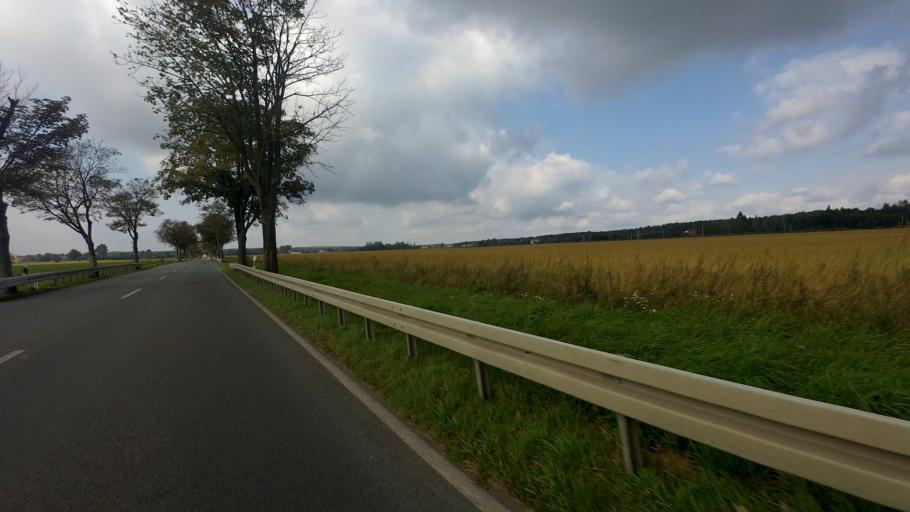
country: DE
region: Brandenburg
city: Plessa
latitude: 51.4690
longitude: 13.5814
